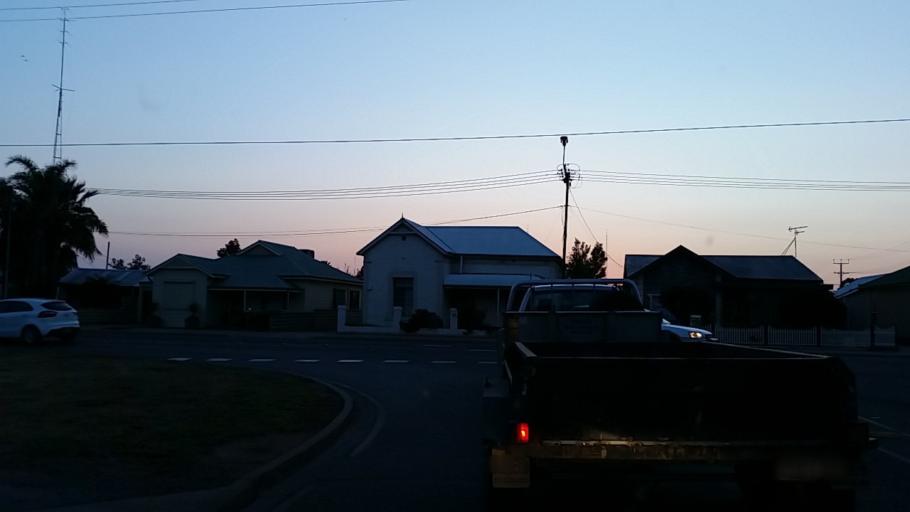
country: AU
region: South Australia
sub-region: Port Pirie City and Dists
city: Port Pirie
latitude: -33.1838
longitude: 138.0042
